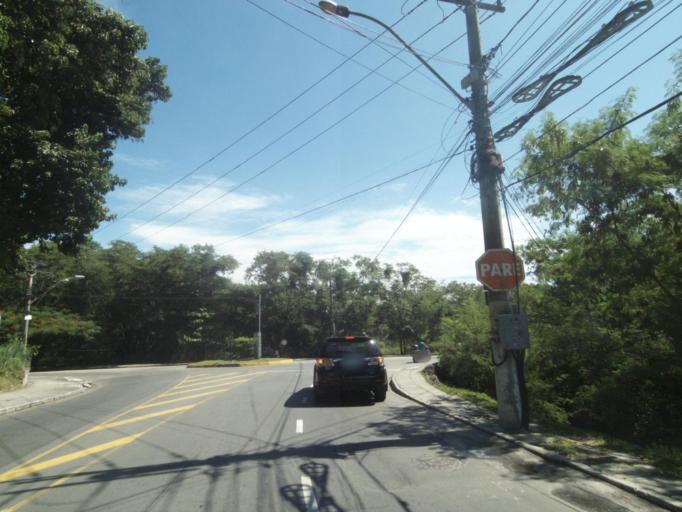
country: BR
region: Rio de Janeiro
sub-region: Niteroi
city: Niteroi
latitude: -22.9504
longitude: -43.0583
